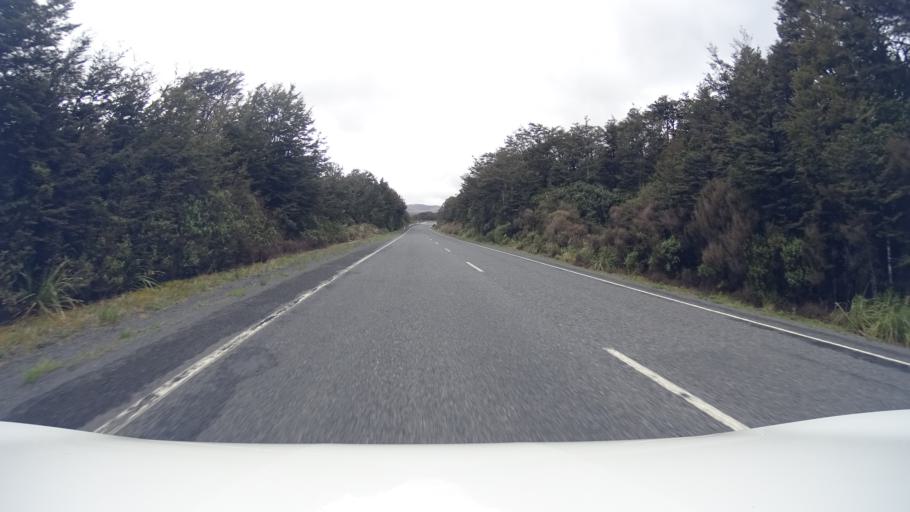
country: NZ
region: Manawatu-Wanganui
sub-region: Ruapehu District
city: Waiouru
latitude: -39.1805
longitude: 175.5222
